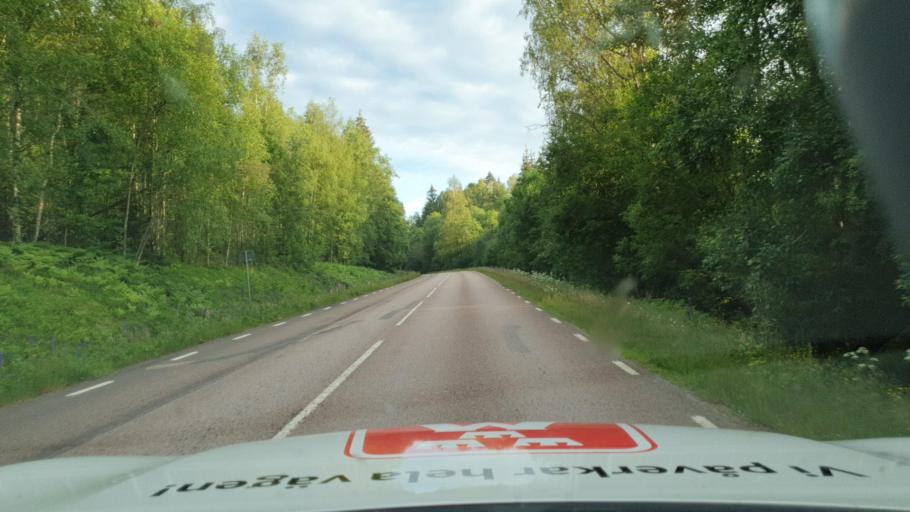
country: SE
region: Vaermland
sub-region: Karlstads Kommun
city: Molkom
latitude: 59.5189
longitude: 13.7957
